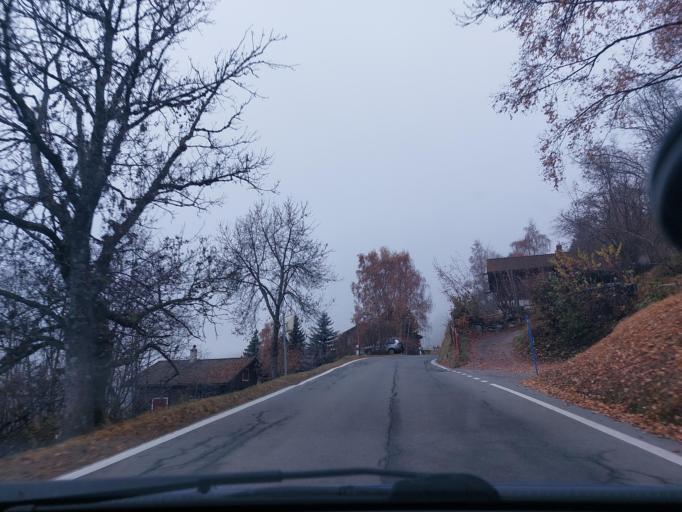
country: CH
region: Valais
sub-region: Conthey District
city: Basse-Nendaz
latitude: 46.1759
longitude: 7.3136
